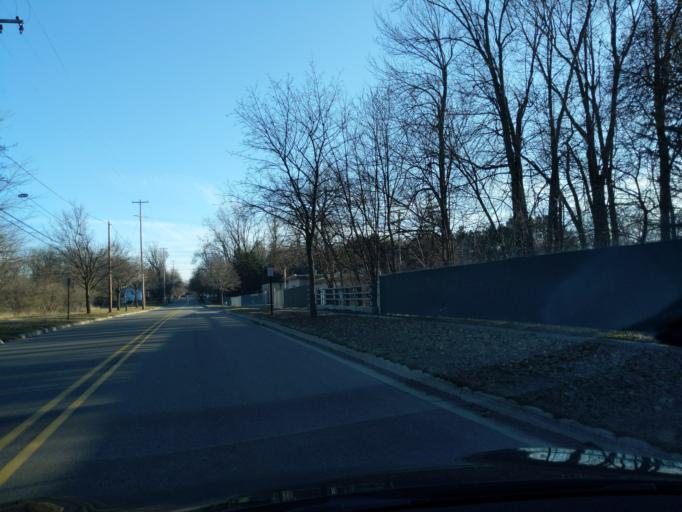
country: US
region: Michigan
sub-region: Ingham County
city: Mason
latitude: 42.5879
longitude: -84.4431
